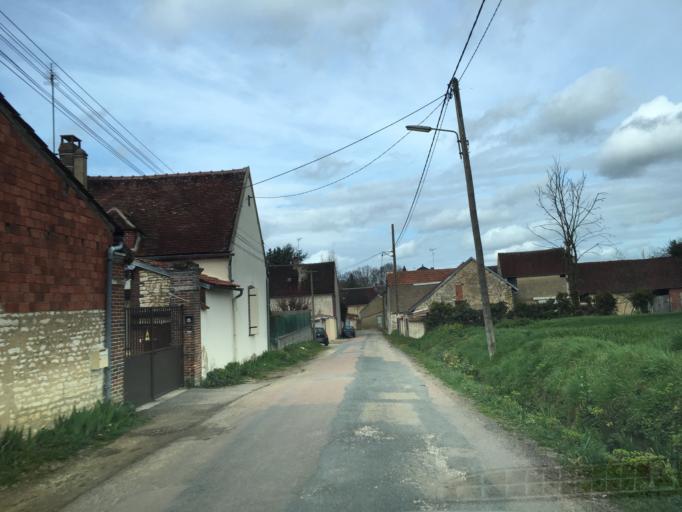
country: FR
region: Bourgogne
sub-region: Departement de l'Yonne
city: Fleury-la-Vallee
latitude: 47.8574
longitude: 3.4074
